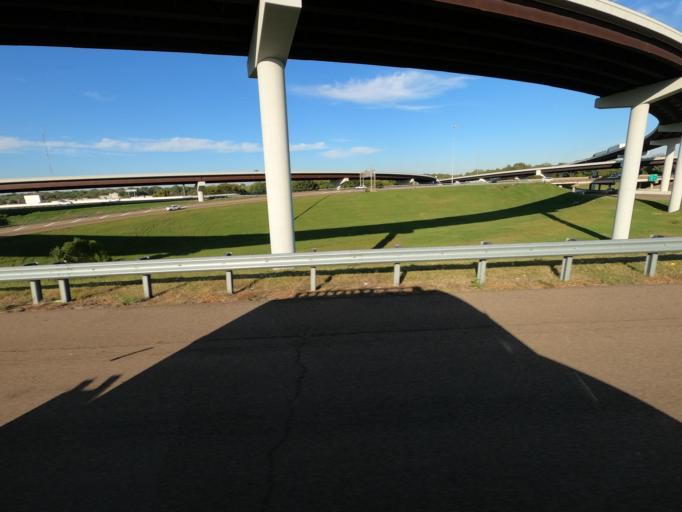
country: US
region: Tennessee
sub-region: Shelby County
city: Bartlett
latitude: 35.1521
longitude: -89.8858
